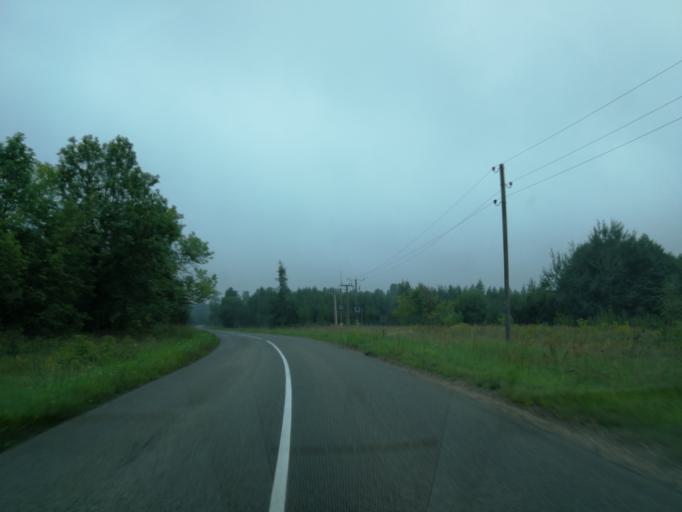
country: LV
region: Preilu Rajons
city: Jaunaglona
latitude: 56.2668
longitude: 27.0239
